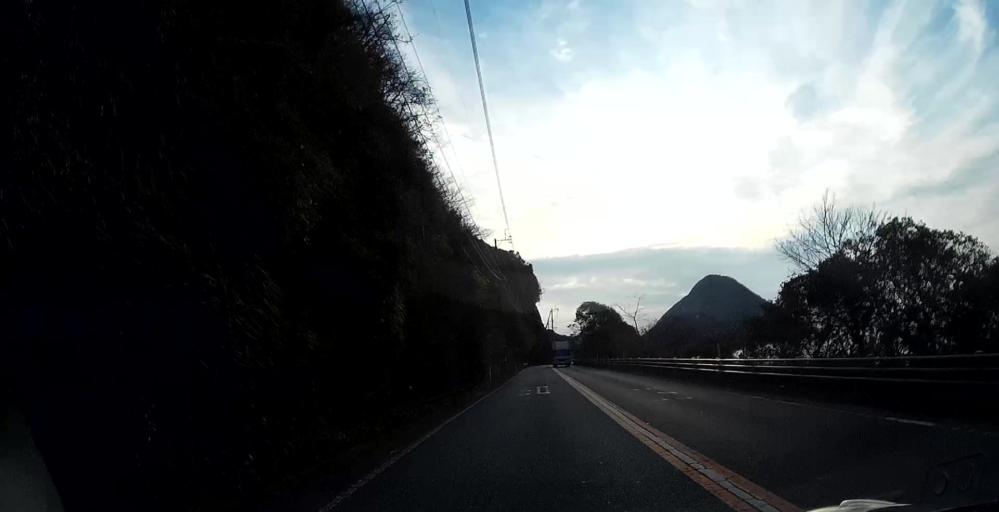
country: JP
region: Nagasaki
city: Shimabara
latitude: 32.6318
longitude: 130.4593
